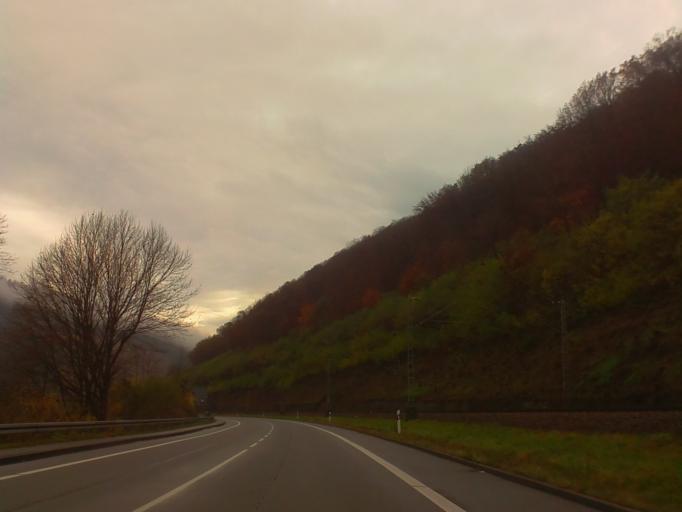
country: DE
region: Hesse
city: Hirschhorn
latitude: 49.4329
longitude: 8.8933
